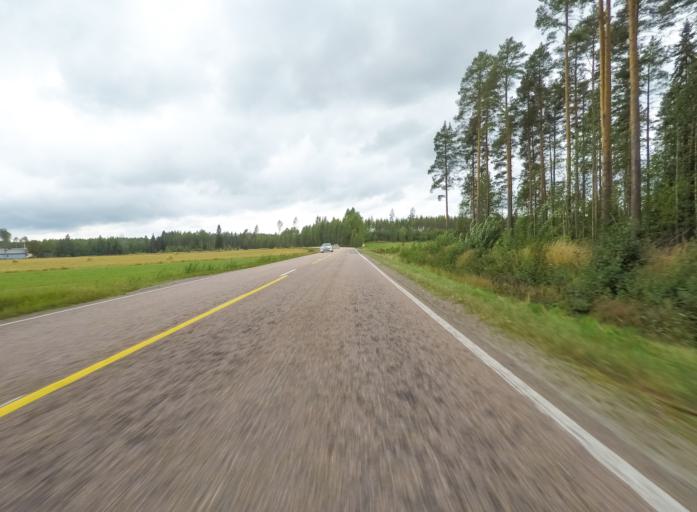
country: FI
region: Central Finland
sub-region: Jyvaeskylae
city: Hankasalmi
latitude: 62.3608
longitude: 26.5456
